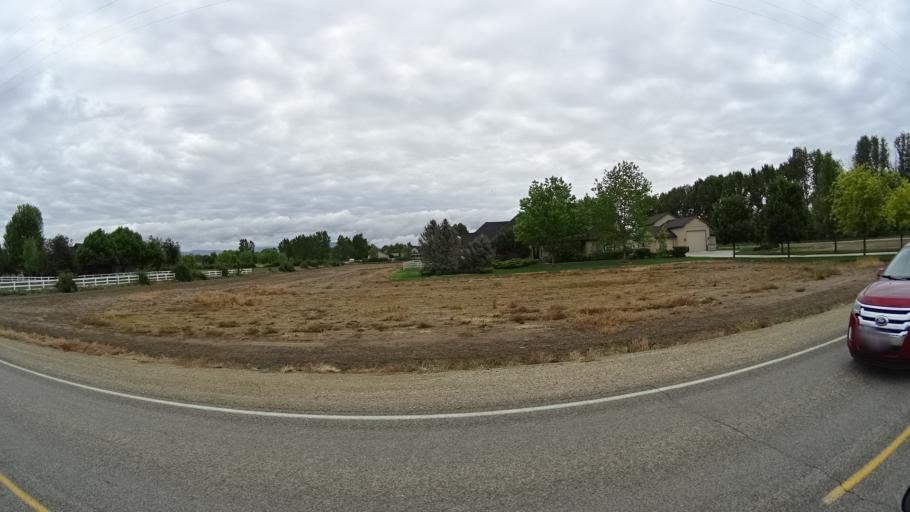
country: US
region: Idaho
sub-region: Ada County
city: Eagle
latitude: 43.7169
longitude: -116.4136
